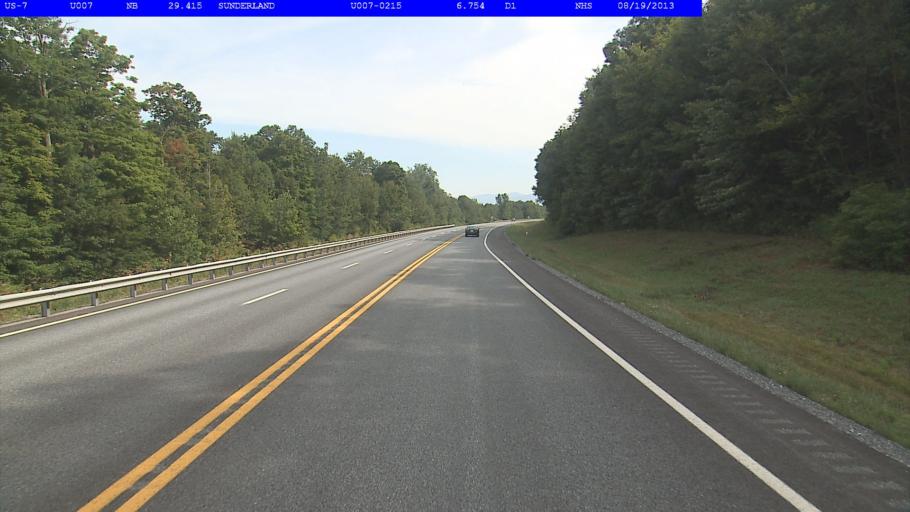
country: US
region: Vermont
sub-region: Bennington County
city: Manchester Center
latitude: 43.1139
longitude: -73.0868
